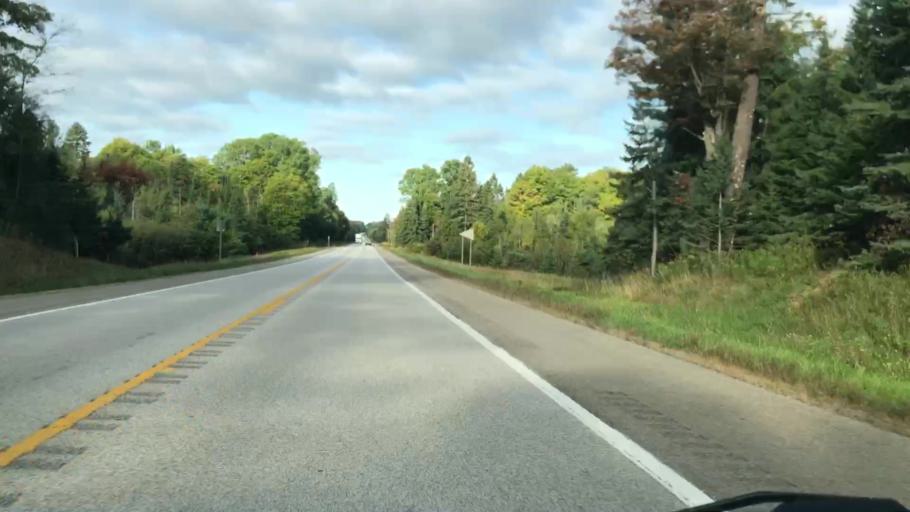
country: US
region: Michigan
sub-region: Luce County
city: Newberry
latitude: 46.3319
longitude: -85.0598
